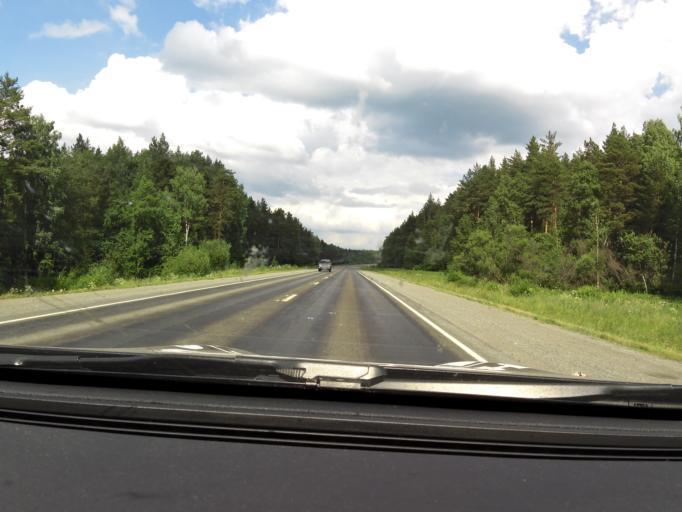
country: RU
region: Sverdlovsk
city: Bisert'
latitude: 56.8262
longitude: 58.7693
